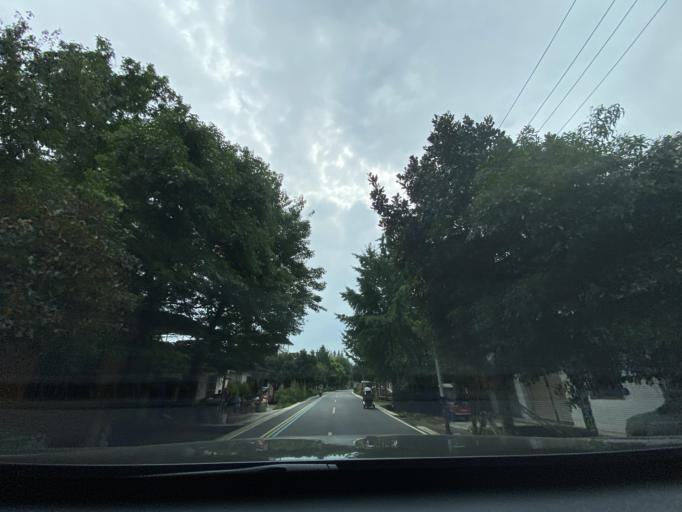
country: CN
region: Sichuan
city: Wujin
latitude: 30.3992
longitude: 103.9869
